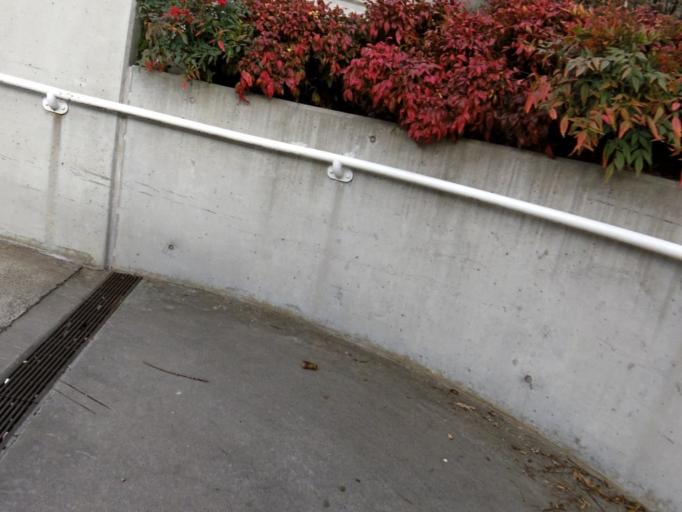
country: AU
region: Australian Capital Territory
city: Kaleen
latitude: -35.2469
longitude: 149.1022
